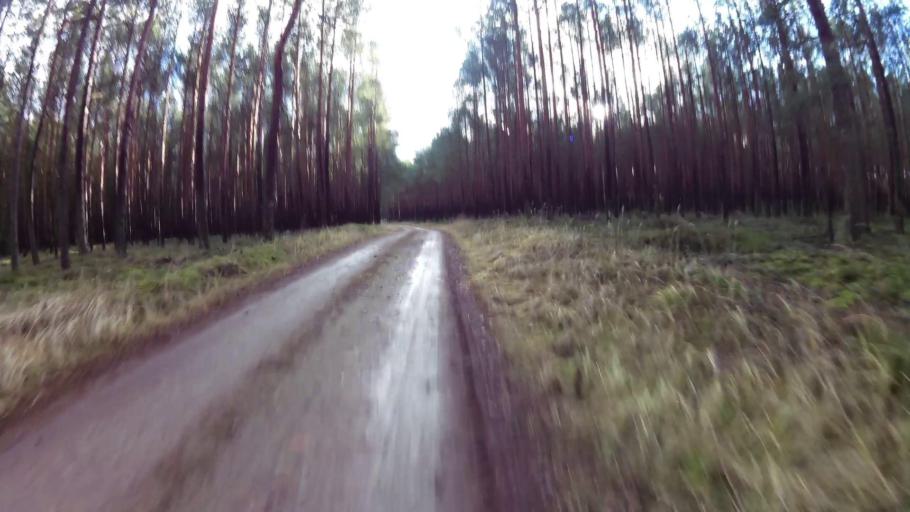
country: PL
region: West Pomeranian Voivodeship
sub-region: Powiat koszalinski
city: Sianow
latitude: 54.1047
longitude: 16.2979
